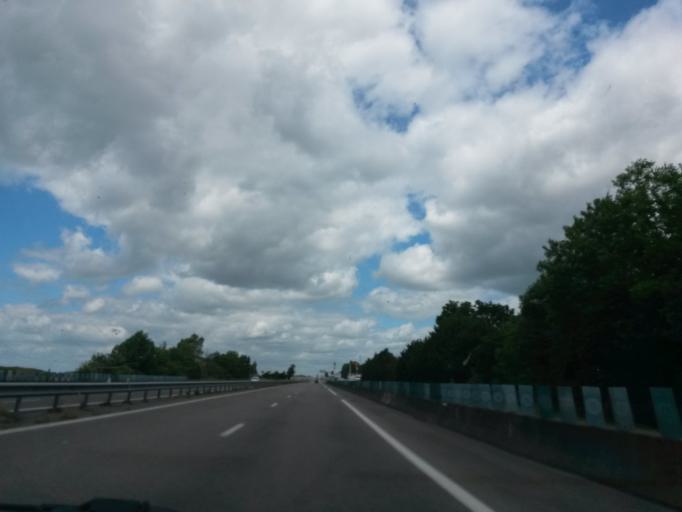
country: FR
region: Bourgogne
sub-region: Departement de la Nievre
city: Cosne-Cours-sur-Loire
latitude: 47.3761
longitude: 2.9231
